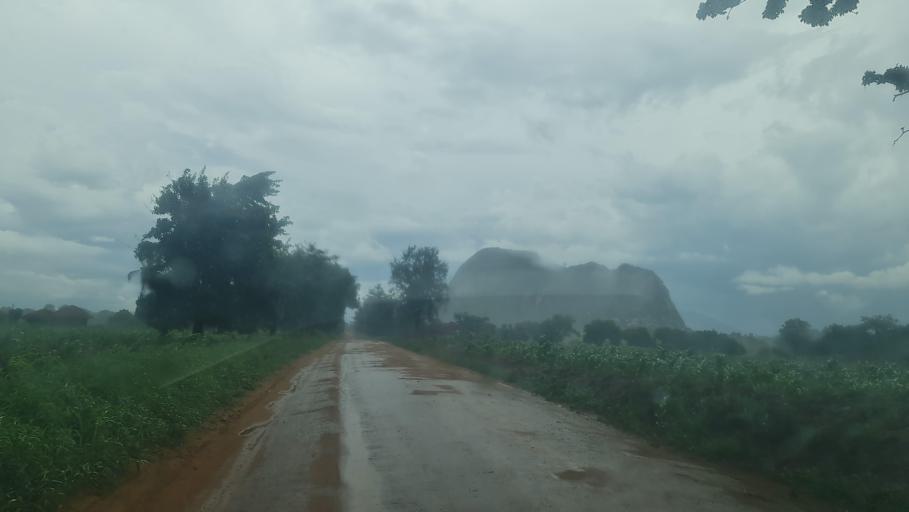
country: MW
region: Southern Region
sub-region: Nsanje District
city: Nsanje
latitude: -17.4010
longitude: 35.5914
